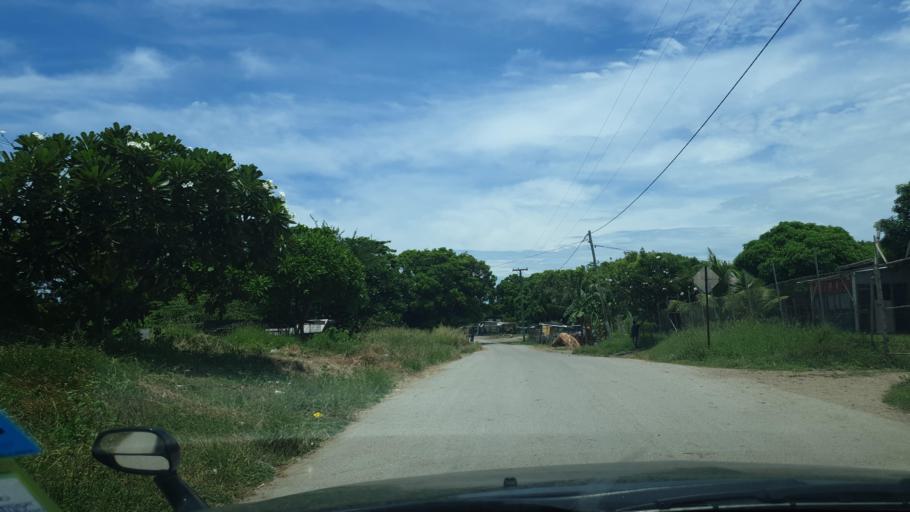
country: PG
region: National Capital
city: Port Moresby
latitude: -9.4230
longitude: 147.0486
